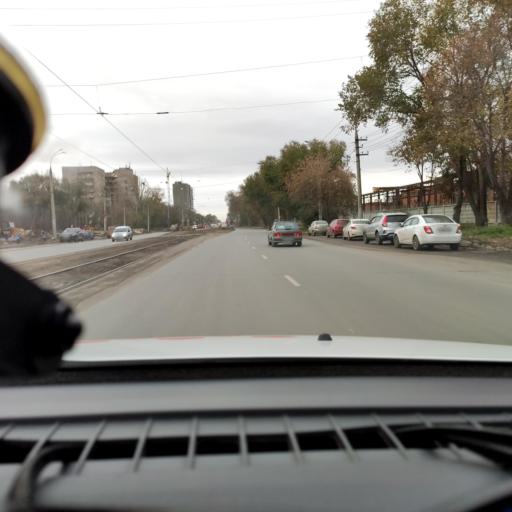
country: RU
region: Samara
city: Smyshlyayevka
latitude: 53.2063
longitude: 50.2783
